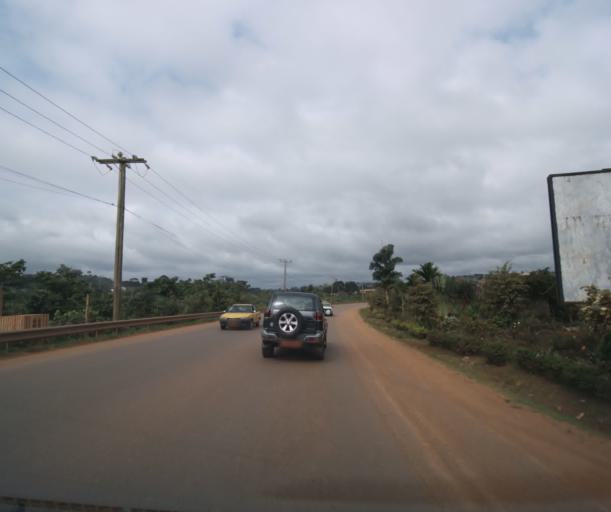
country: CM
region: Centre
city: Yaounde
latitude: 3.8031
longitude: 11.5109
